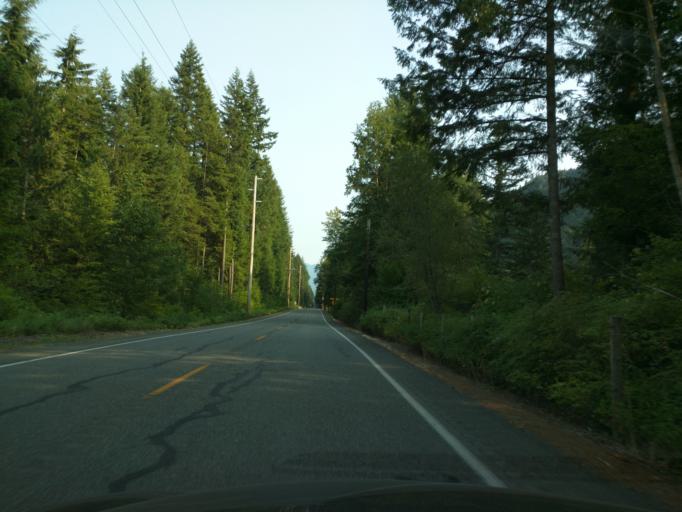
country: US
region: Washington
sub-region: Whatcom County
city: Peaceful Valley
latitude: 48.9602
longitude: -122.1591
